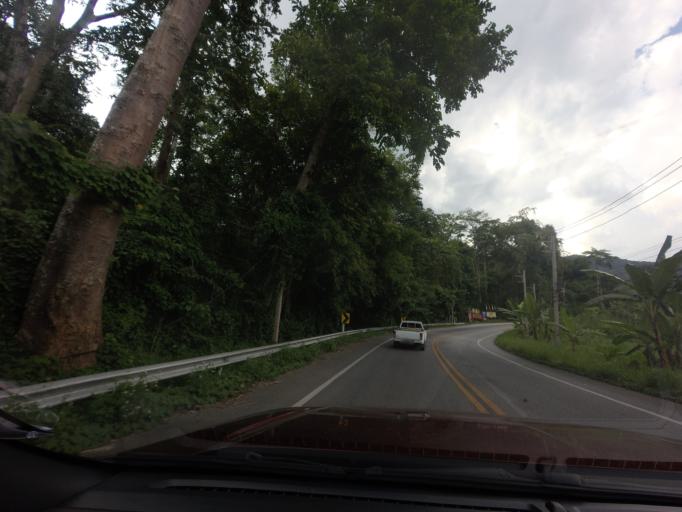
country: TH
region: Yala
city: Than To
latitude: 6.1985
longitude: 101.1734
